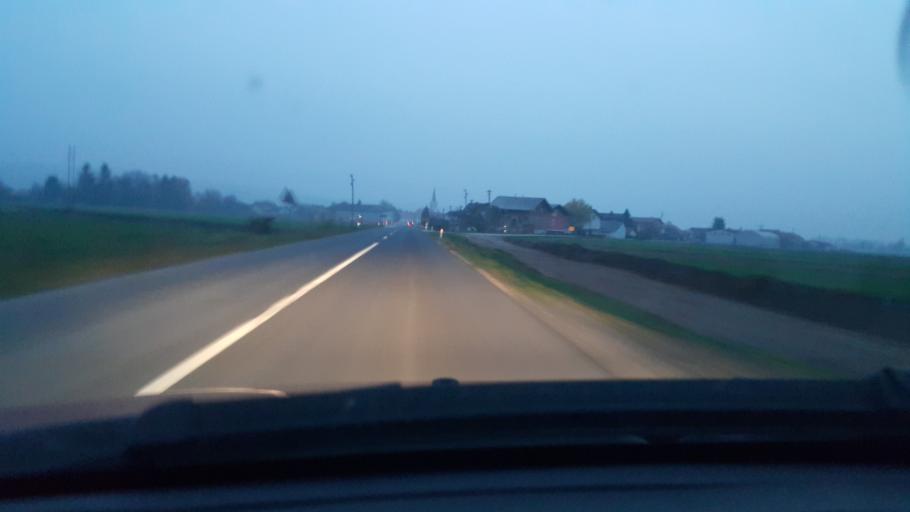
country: SI
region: Kidricevo
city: Kidricevo
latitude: 46.3780
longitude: 15.7858
